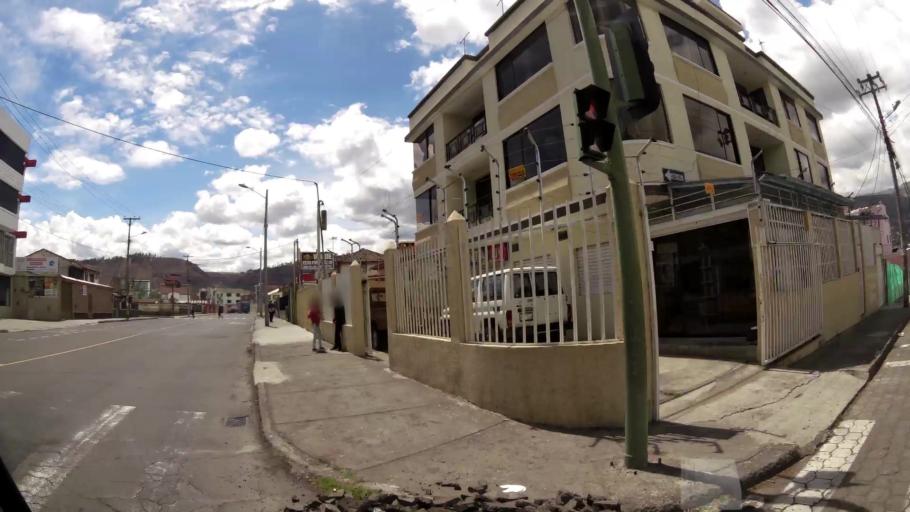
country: EC
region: Tungurahua
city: Ambato
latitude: -1.2482
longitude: -78.6286
